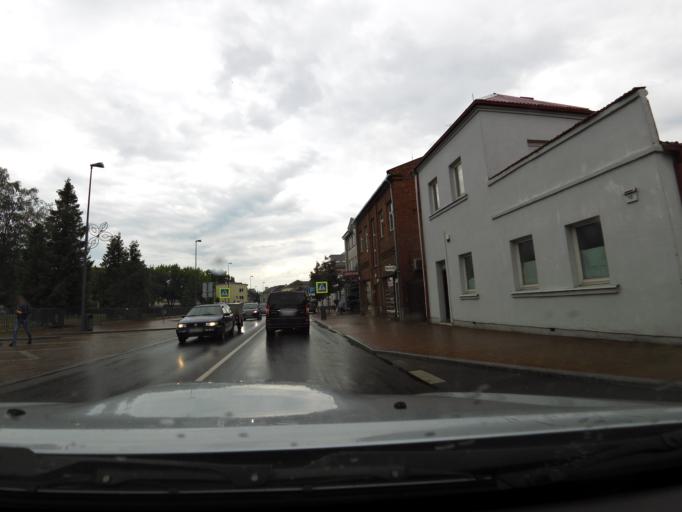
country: LT
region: Marijampoles apskritis
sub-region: Marijampole Municipality
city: Marijampole
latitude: 54.5550
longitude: 23.3521
